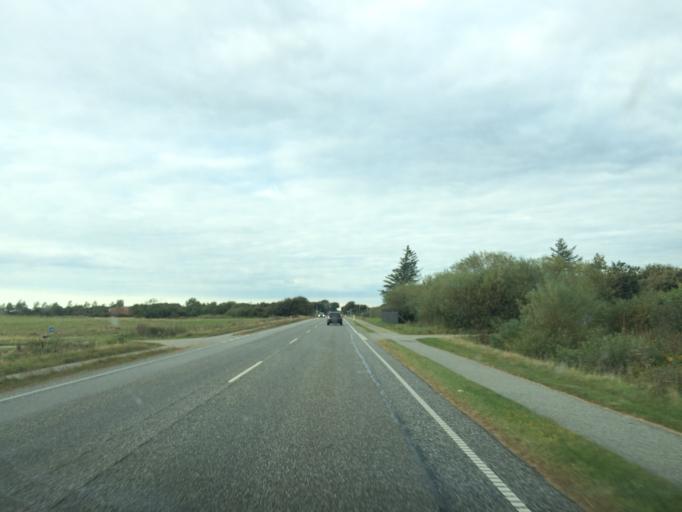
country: DK
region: Central Jutland
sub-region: Ringkobing-Skjern Kommune
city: Ringkobing
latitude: 56.1392
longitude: 8.2819
